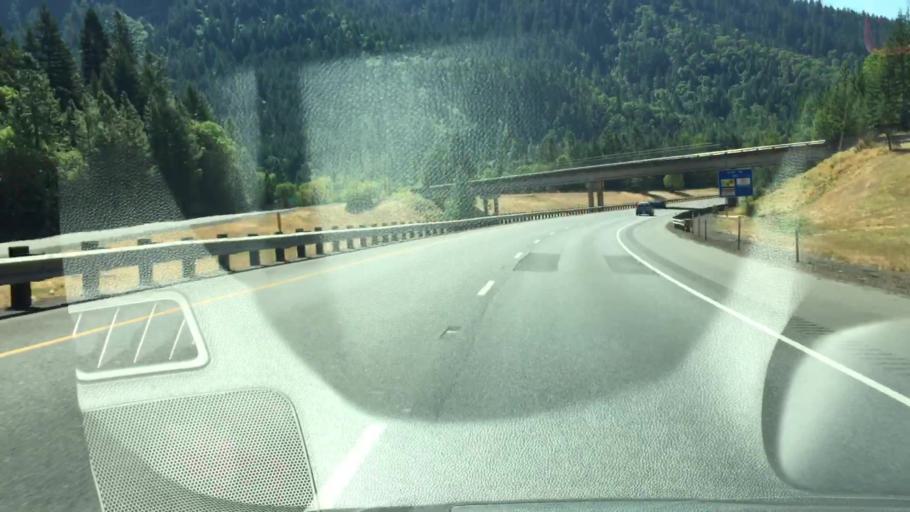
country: US
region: Oregon
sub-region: Josephine County
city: Merlin
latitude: 42.7122
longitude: -123.3658
